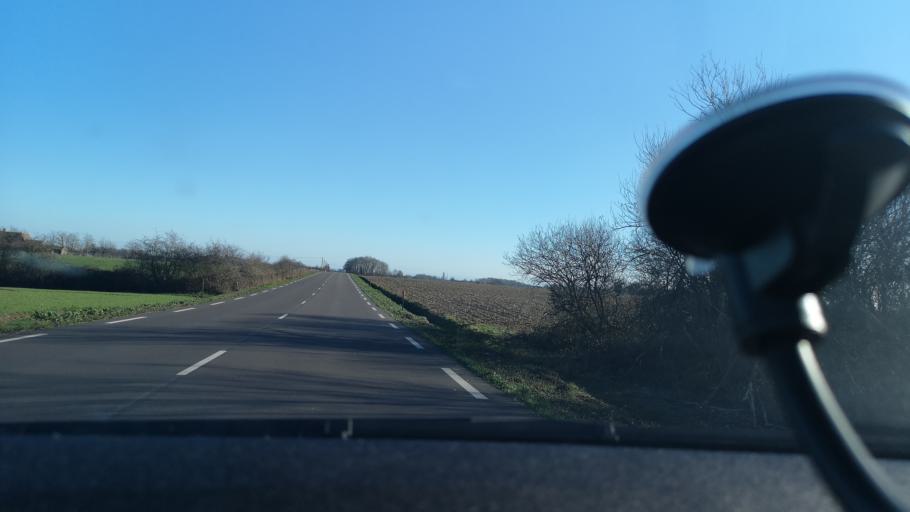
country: FR
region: Bourgogne
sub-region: Departement de Saone-et-Loire
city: Saint-Martin-en-Bresse
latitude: 46.7451
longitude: 5.0617
